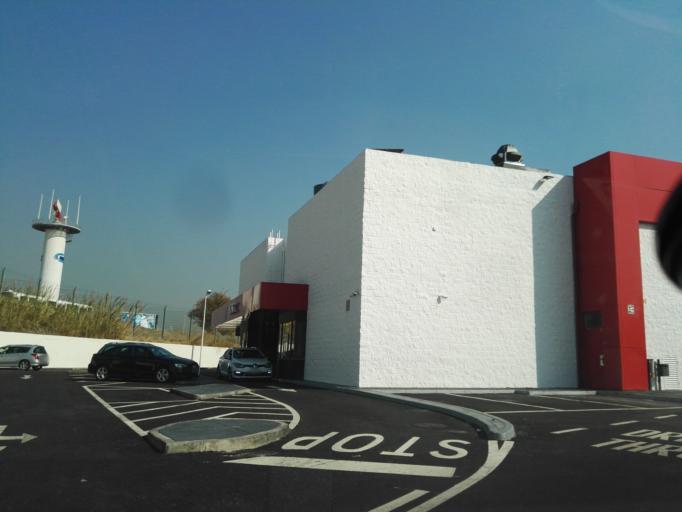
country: PT
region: Lisbon
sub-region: Odivelas
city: Olival do Basto
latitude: 38.7636
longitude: -9.1407
